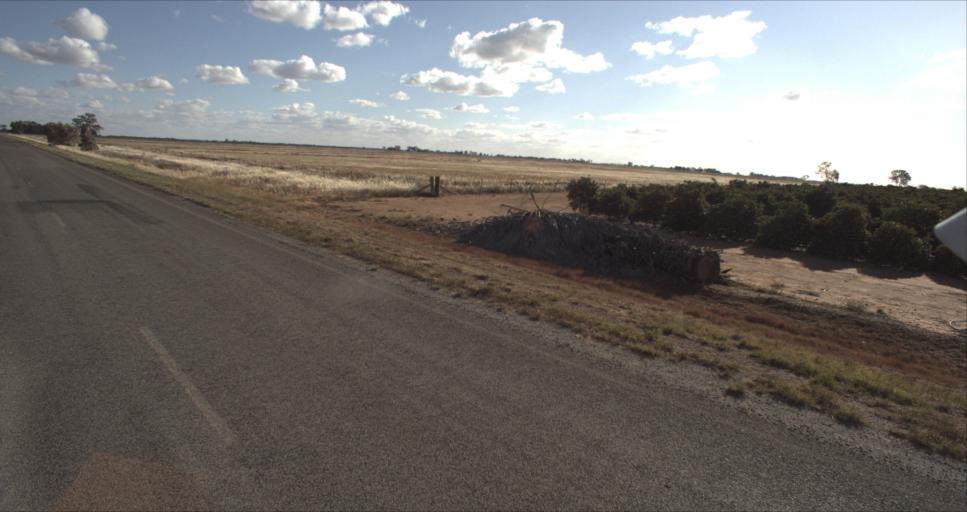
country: AU
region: New South Wales
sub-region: Leeton
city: Leeton
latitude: -34.5296
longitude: 146.2817
